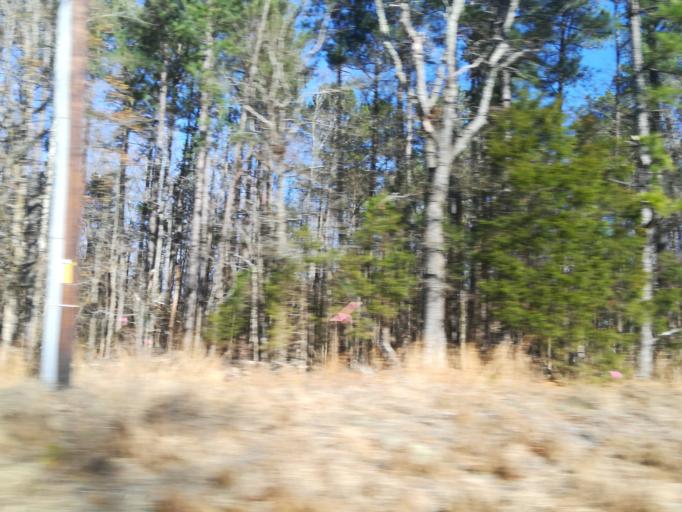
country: US
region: North Carolina
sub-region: Durham County
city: Durham
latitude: 36.0323
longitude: -78.9891
